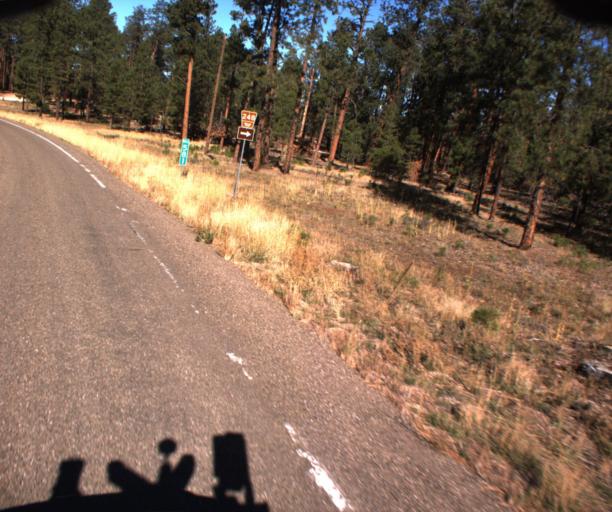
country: US
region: Arizona
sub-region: Coconino County
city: Fredonia
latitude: 36.7362
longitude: -112.2153
